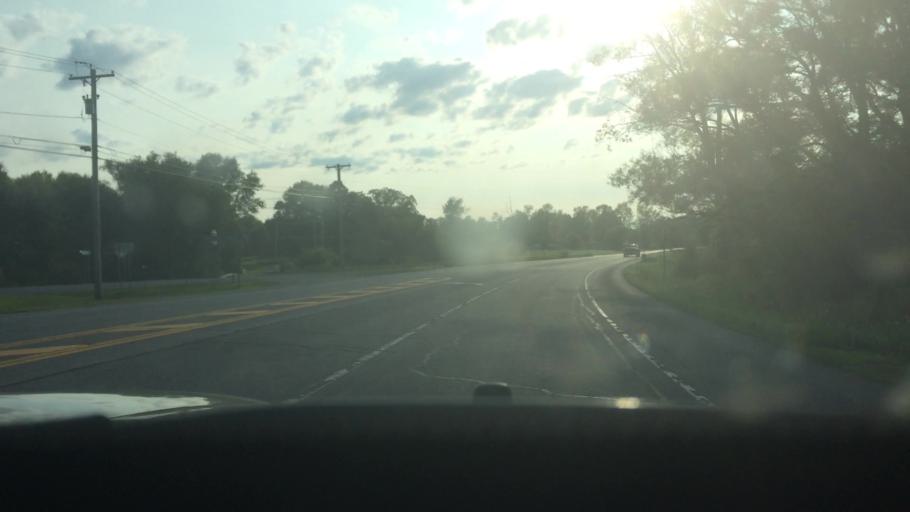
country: US
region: New York
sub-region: St. Lawrence County
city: Ogdensburg
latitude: 44.6721
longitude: -75.4235
